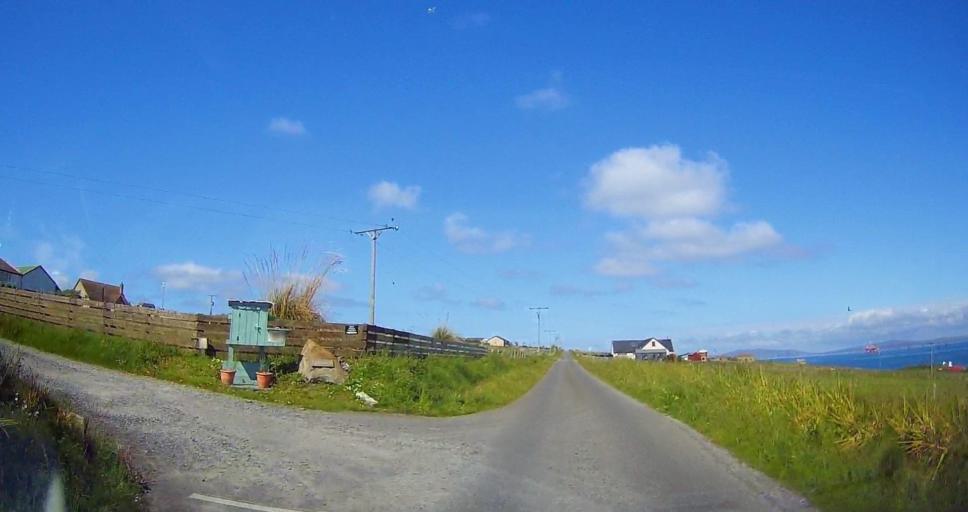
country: GB
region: Scotland
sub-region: Orkney Islands
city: Kirkwall
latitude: 58.8538
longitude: -2.9220
